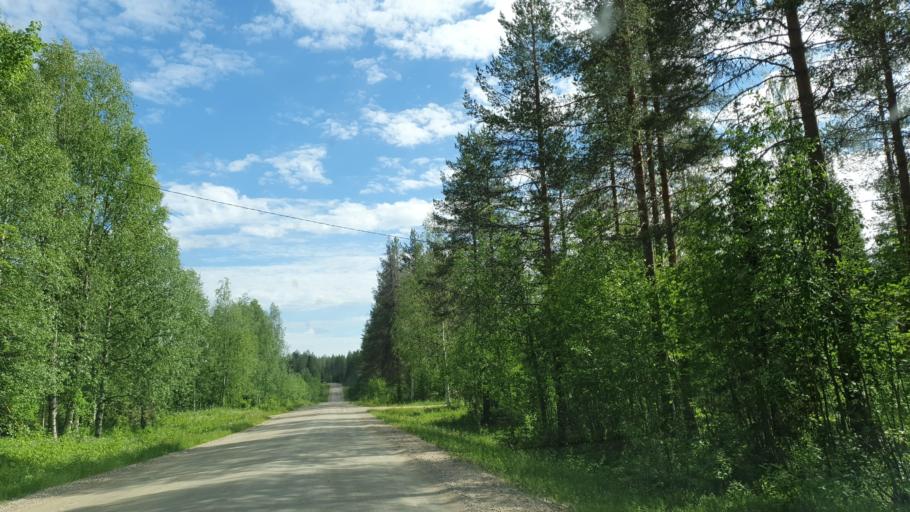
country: FI
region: Kainuu
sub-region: Kehys-Kainuu
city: Kuhmo
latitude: 64.4964
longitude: 29.4911
